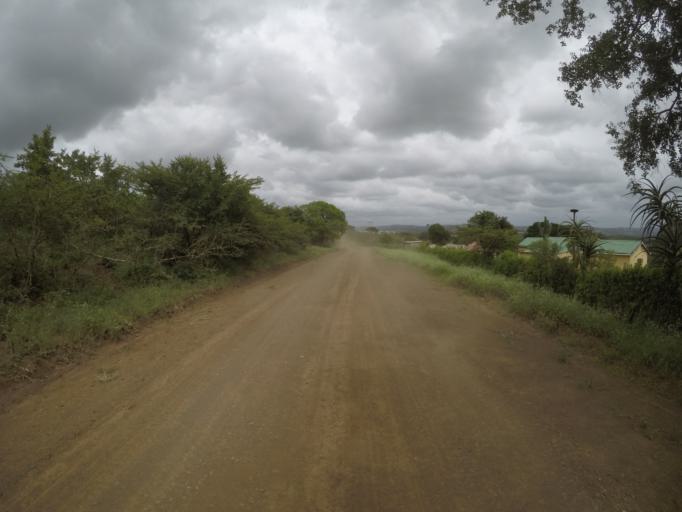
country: ZA
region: KwaZulu-Natal
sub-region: uThungulu District Municipality
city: Empangeni
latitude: -28.5775
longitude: 31.8705
